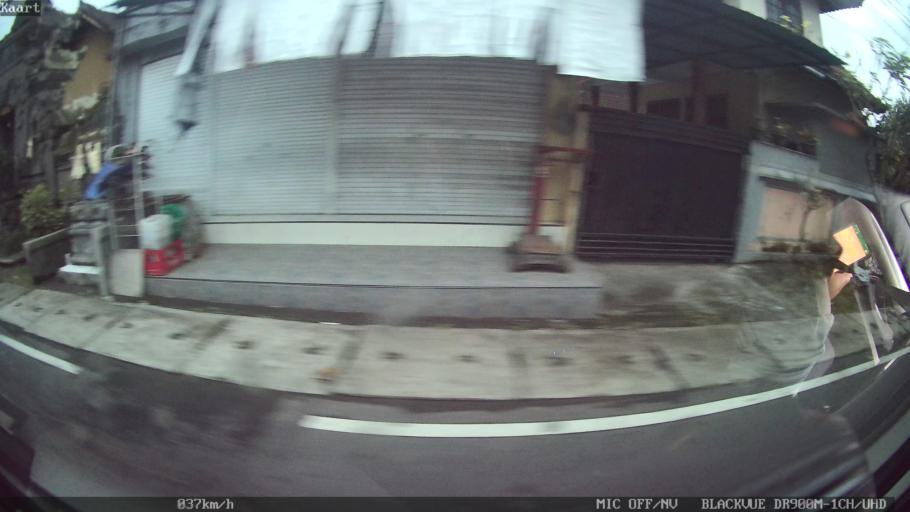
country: ID
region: Bali
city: Banjar Sayanbaleran
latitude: -8.5178
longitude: 115.1872
